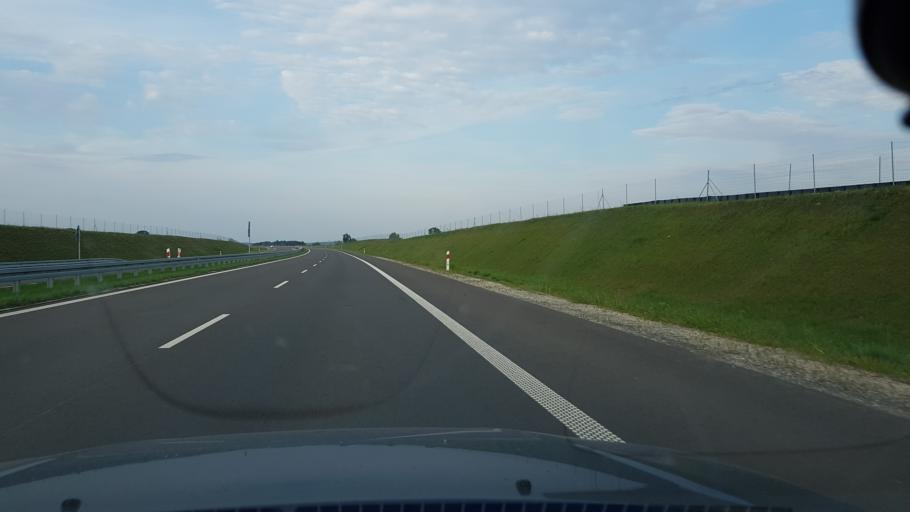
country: PL
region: Lower Silesian Voivodeship
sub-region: Powiat jaworski
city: Paszowice
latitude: 50.9373
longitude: 16.1771
